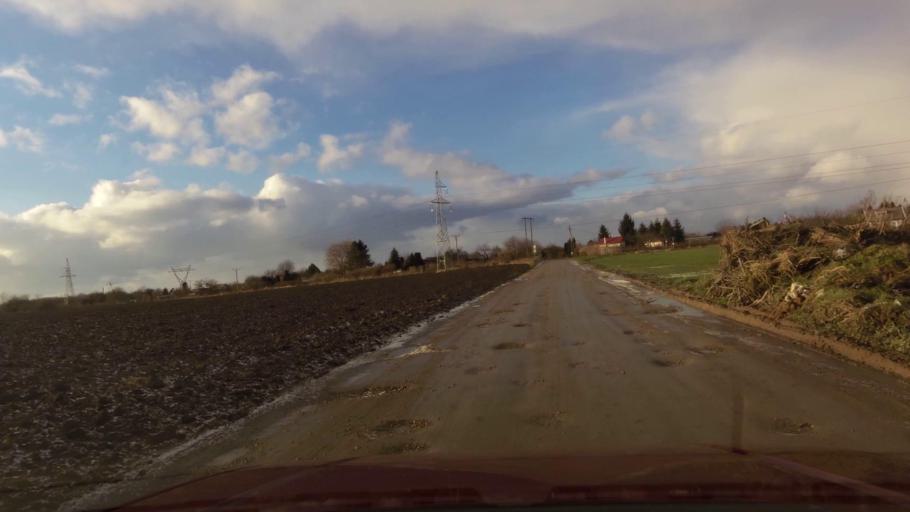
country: PL
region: West Pomeranian Voivodeship
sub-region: Koszalin
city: Koszalin
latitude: 54.1683
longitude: 16.1694
